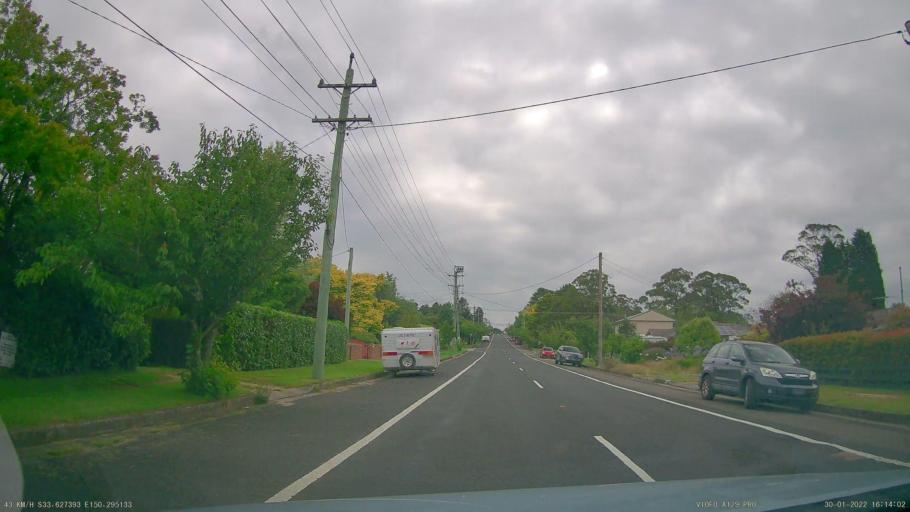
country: AU
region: New South Wales
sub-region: Blue Mountains Municipality
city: Blackheath
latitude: -33.6275
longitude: 150.2950
